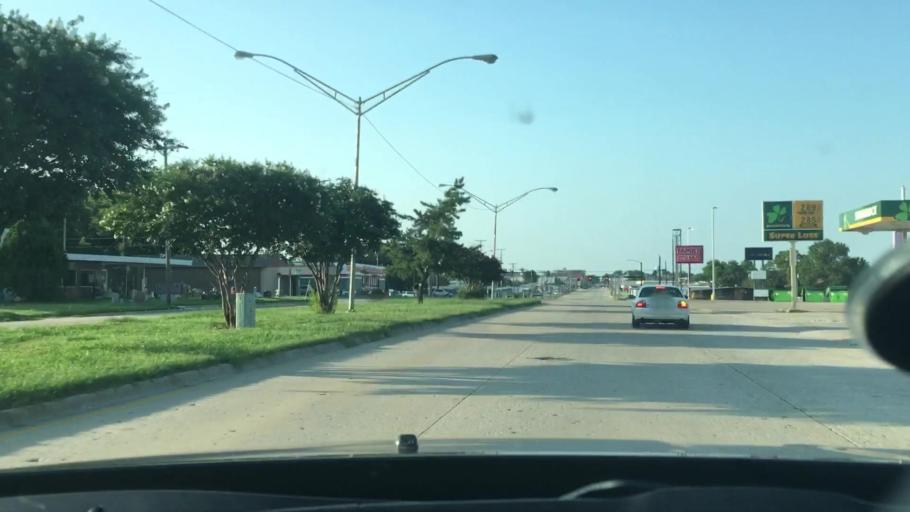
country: US
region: Oklahoma
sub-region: Pontotoc County
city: Ada
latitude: 34.7836
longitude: -96.6788
